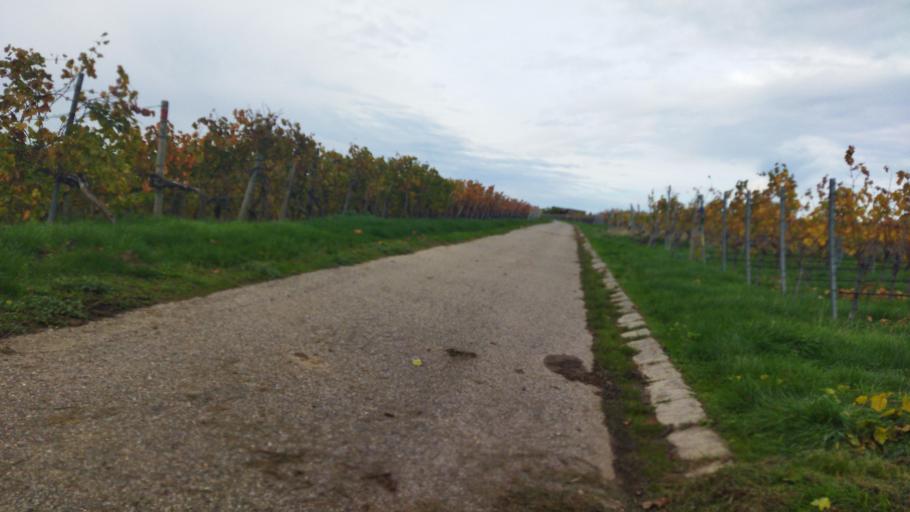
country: DE
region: Baden-Wuerttemberg
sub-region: Regierungsbezirk Stuttgart
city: Gemmrigheim
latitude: 49.0352
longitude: 9.1589
